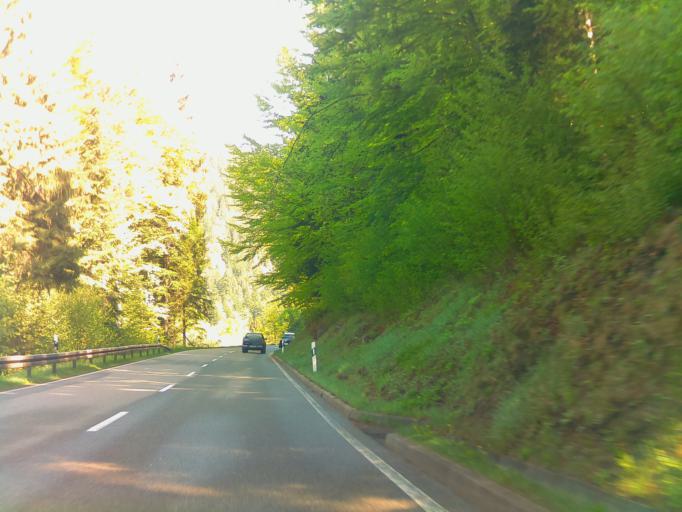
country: DE
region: Baden-Wuerttemberg
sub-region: Karlsruhe Region
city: Bad Wildbad
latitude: 48.7493
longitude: 8.5816
